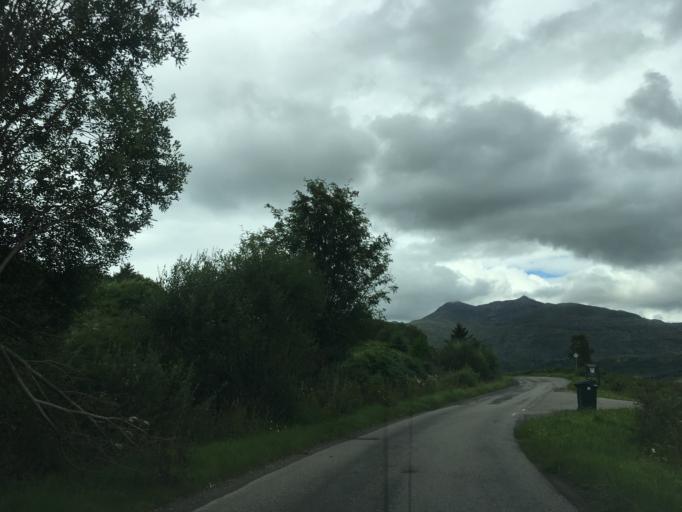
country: GB
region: Scotland
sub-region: Argyll and Bute
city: Oban
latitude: 56.3699
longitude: -5.1778
